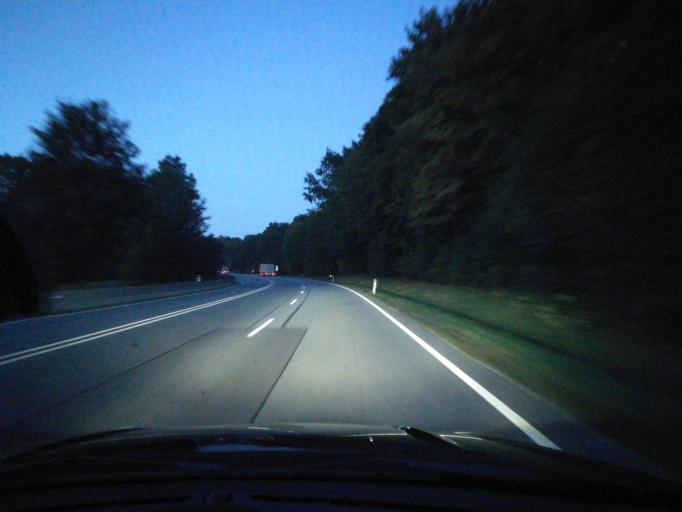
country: DE
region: Bavaria
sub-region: Lower Bavaria
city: Bad Abbach
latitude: 48.9408
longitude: 12.0430
